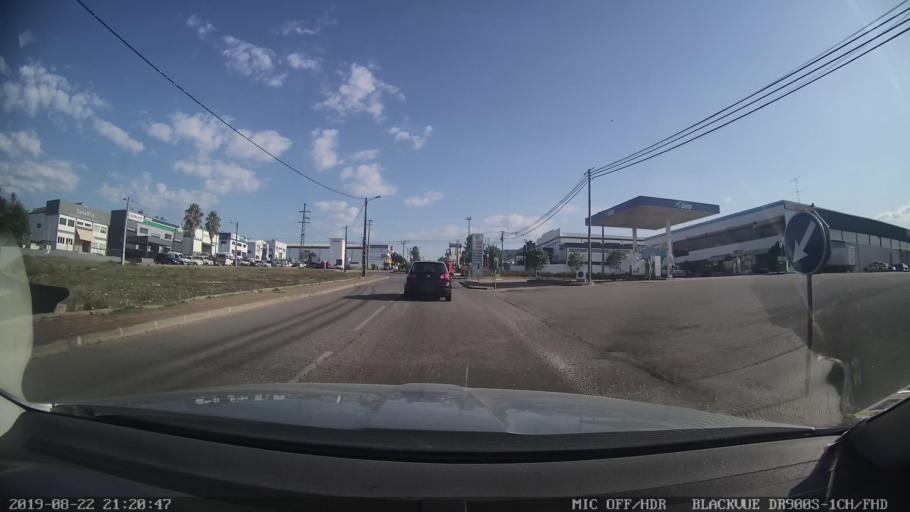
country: PT
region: Castelo Branco
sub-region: Serta
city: Serta
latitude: 39.8147
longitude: -8.1091
